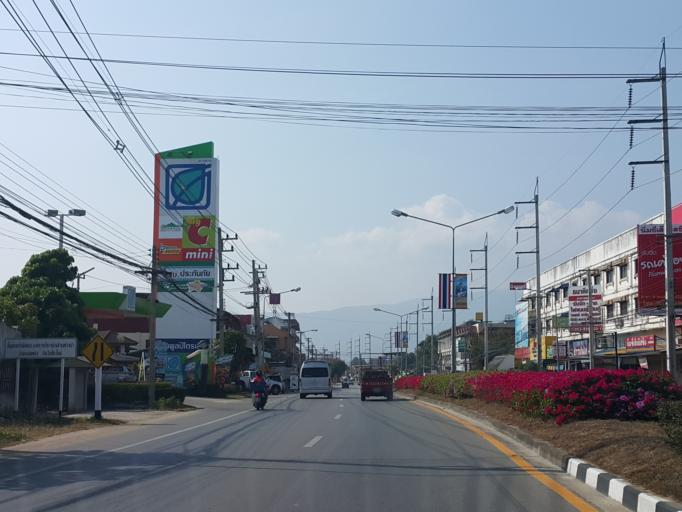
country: TH
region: Chiang Mai
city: Chom Thong
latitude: 18.4318
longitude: 98.6837
